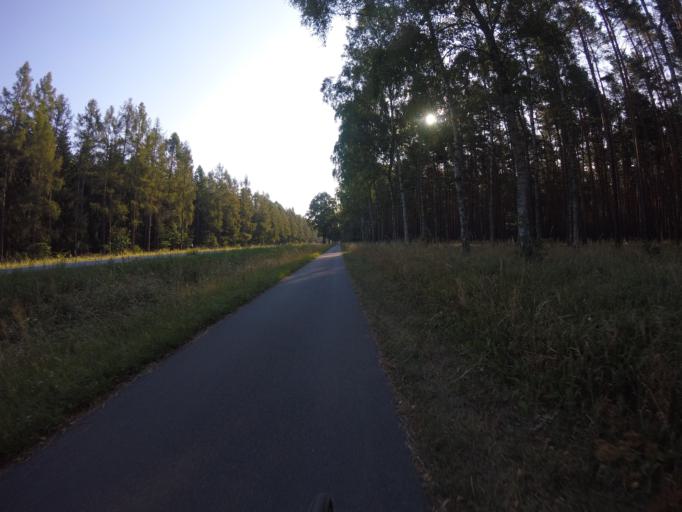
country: DE
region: Brandenburg
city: Spreenhagen
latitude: 52.3979
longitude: 13.8581
